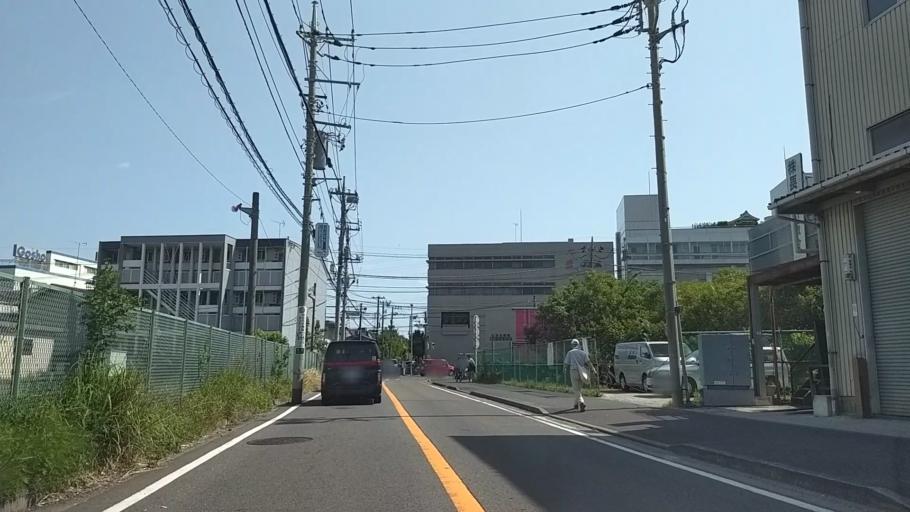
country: JP
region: Kanagawa
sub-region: Kawasaki-shi
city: Kawasaki
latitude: 35.5320
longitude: 139.6470
